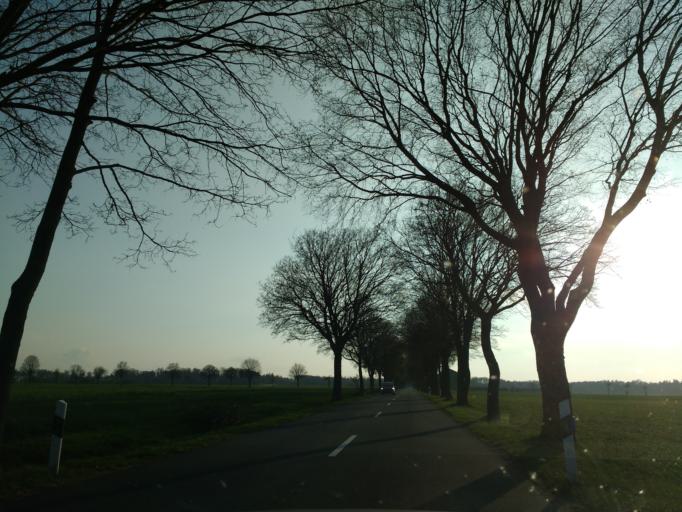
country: DE
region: North Rhine-Westphalia
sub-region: Regierungsbezirk Detmold
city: Paderborn
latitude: 51.6187
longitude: 8.7434
